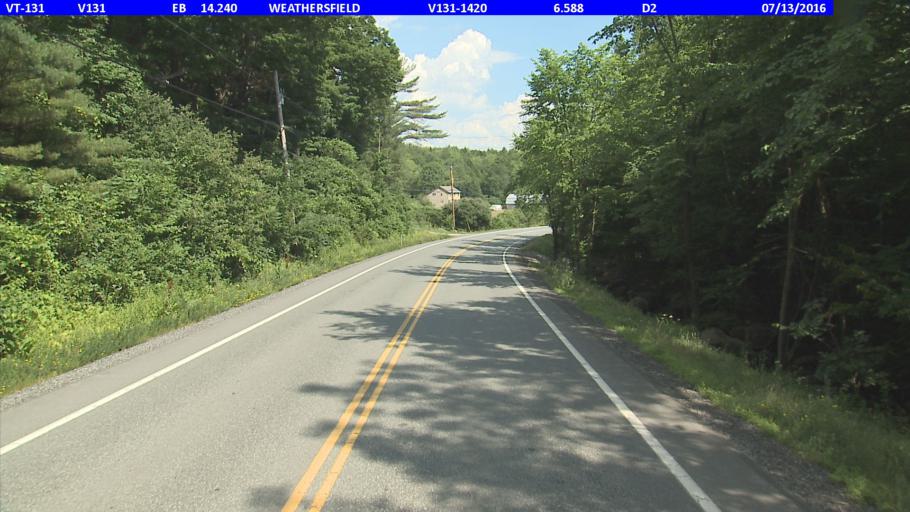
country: US
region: Vermont
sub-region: Windsor County
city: Windsor
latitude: 43.4097
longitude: -72.4424
